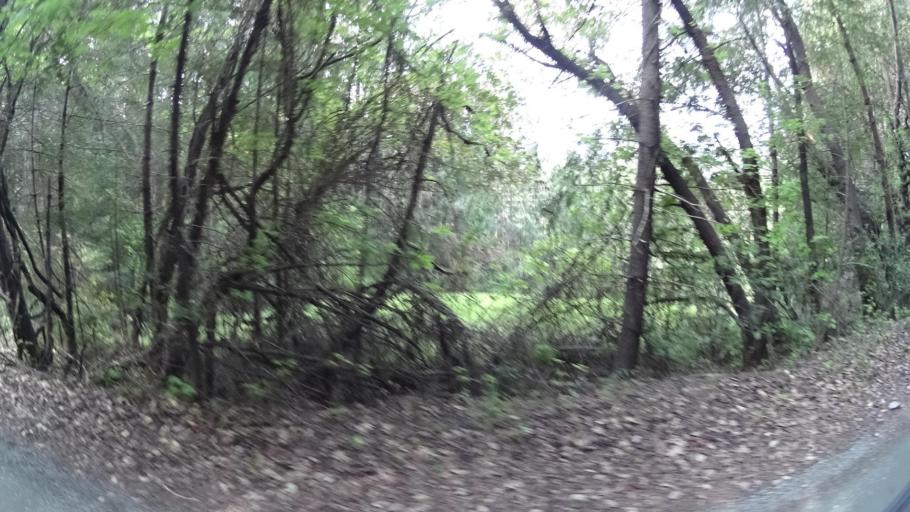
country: US
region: California
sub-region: Humboldt County
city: Redway
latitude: 40.2416
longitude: -123.8137
